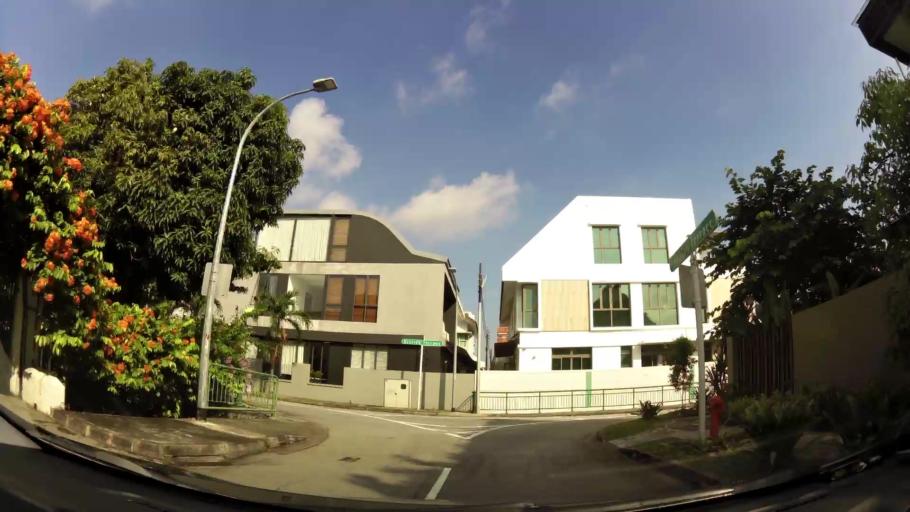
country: SG
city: Singapore
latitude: 1.3126
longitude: 103.9211
